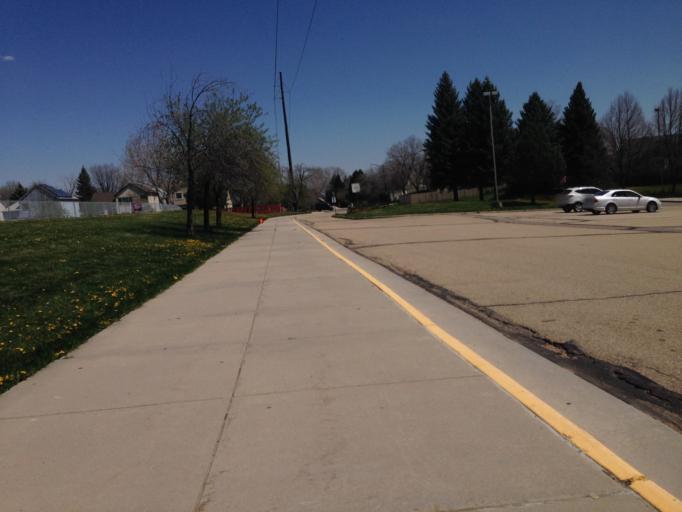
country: US
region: Colorado
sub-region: Boulder County
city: Lafayette
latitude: 39.9906
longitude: -105.1037
